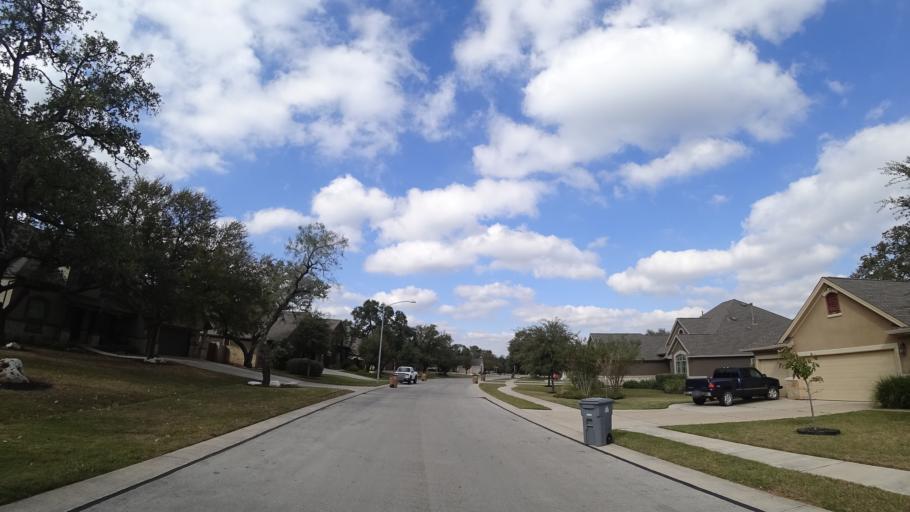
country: US
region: Texas
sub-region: Travis County
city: Shady Hollow
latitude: 30.1745
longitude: -97.8502
